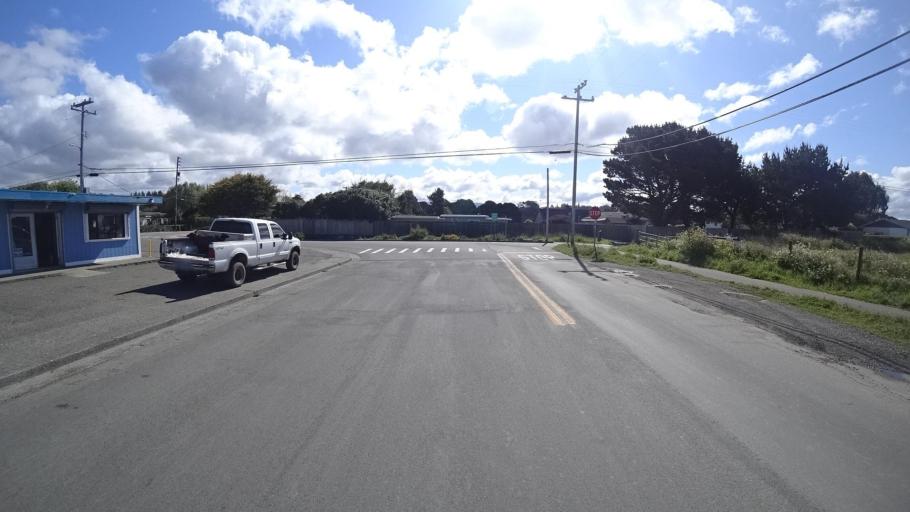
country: US
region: California
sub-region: Humboldt County
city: McKinleyville
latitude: 40.9340
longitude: -124.1205
